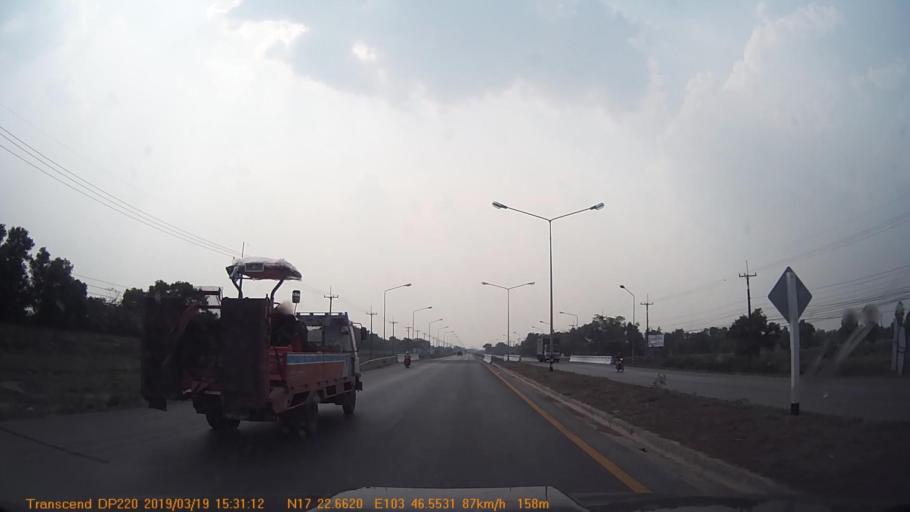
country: TH
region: Sakon Nakhon
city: Phang Khon
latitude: 17.3778
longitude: 103.7753
